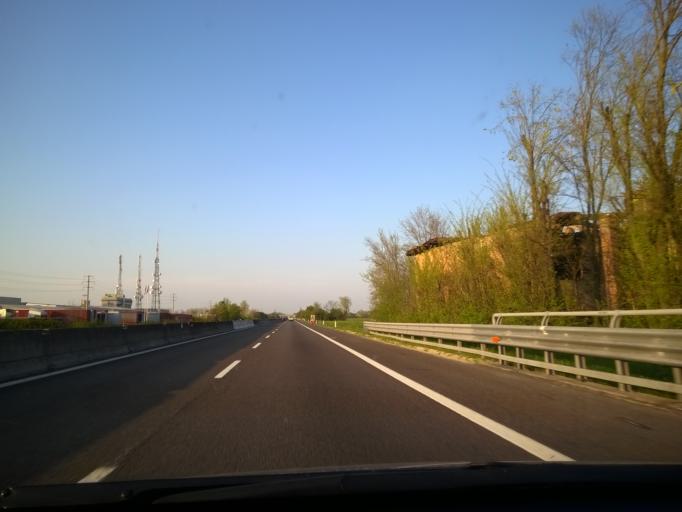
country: IT
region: Emilia-Romagna
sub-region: Provincia di Bologna
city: Progresso
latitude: 44.5554
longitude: 11.3765
